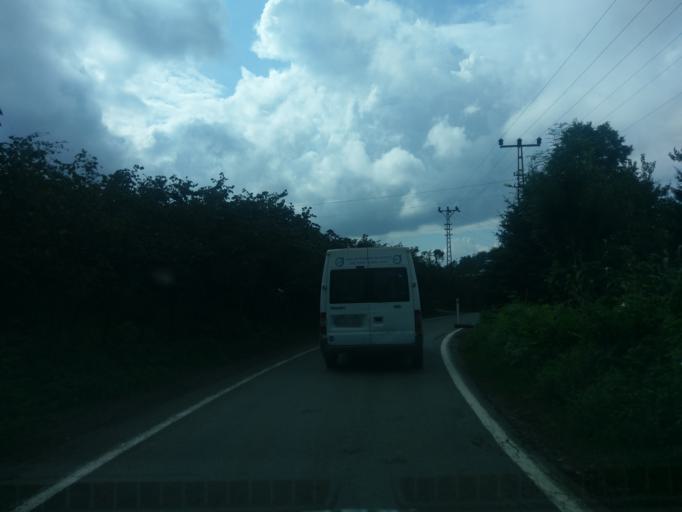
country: TR
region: Ordu
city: Camas
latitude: 40.9107
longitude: 37.6120
